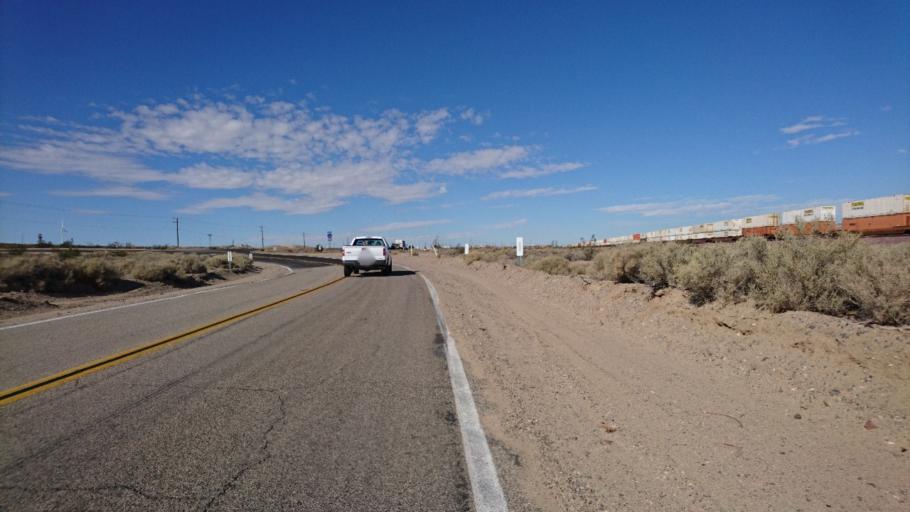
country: US
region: California
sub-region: San Bernardino County
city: Barstow
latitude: 34.8677
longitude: -116.9293
